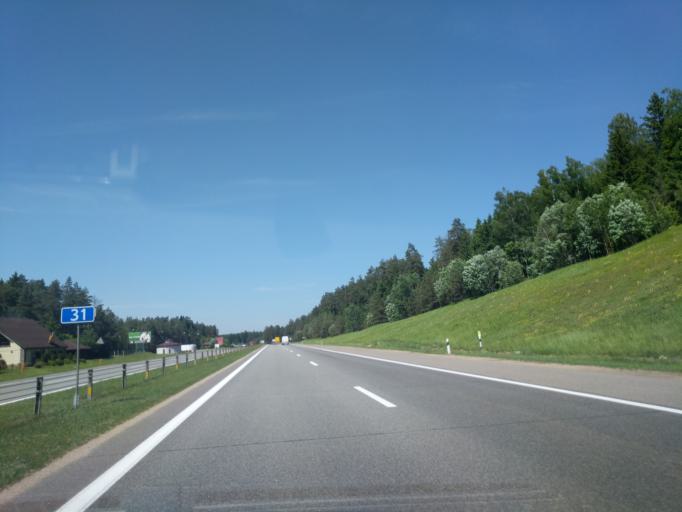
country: BY
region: Minsk
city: Rakaw
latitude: 53.9504
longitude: 27.1182
